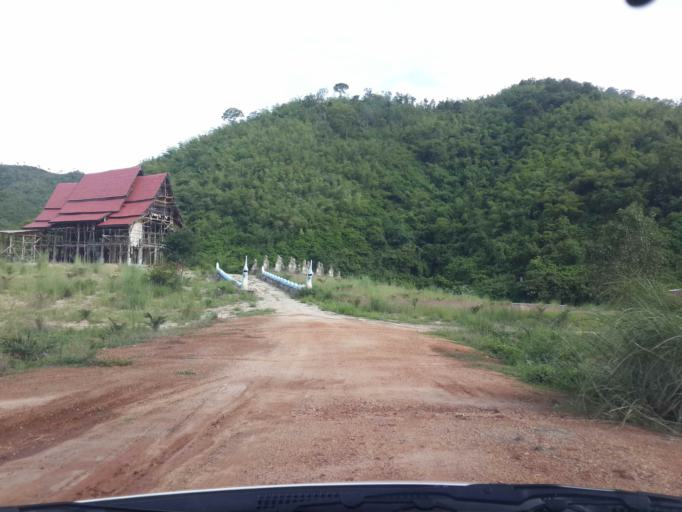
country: TH
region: Kanchanaburi
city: Dan Makham Tia
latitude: 13.7529
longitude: 99.2037
